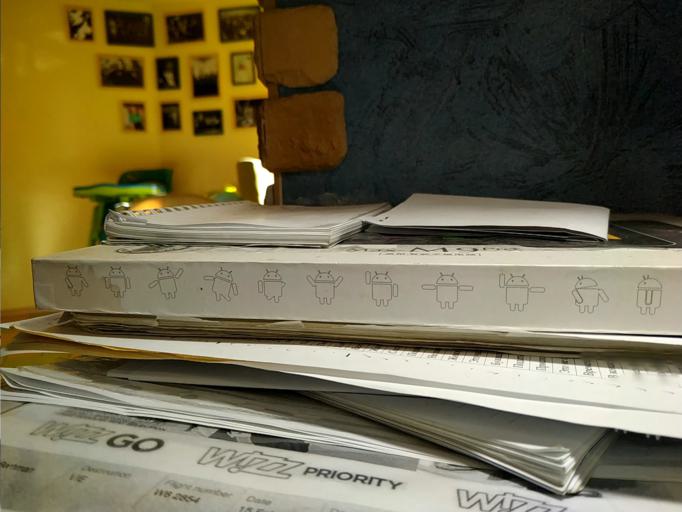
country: RU
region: Novgorod
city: Poddor'ye
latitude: 57.5016
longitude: 30.9437
